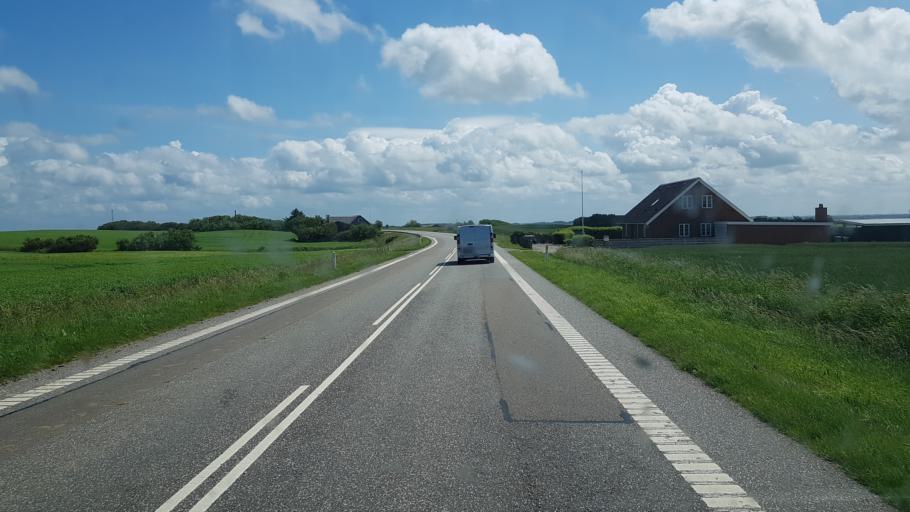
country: DK
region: Central Jutland
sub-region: Lemvig Kommune
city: Lemvig
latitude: 56.5546
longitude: 8.3820
